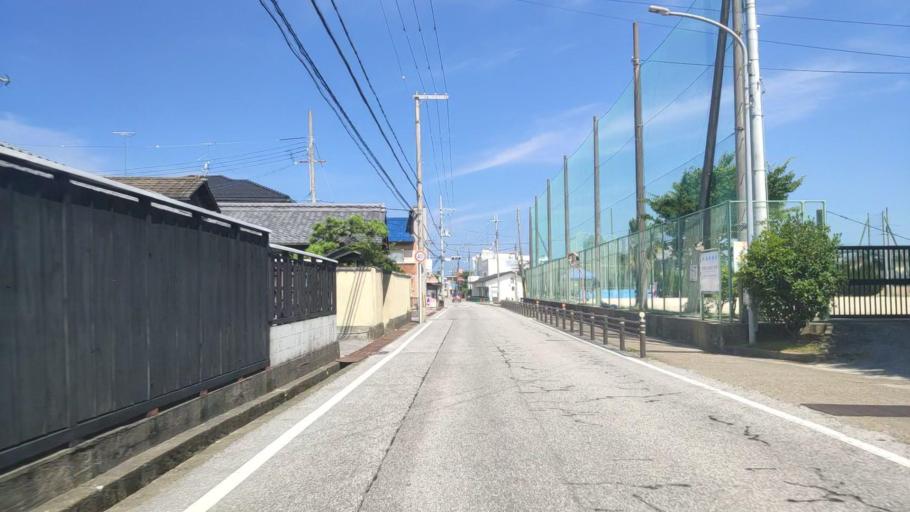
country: JP
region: Shiga Prefecture
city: Hikone
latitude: 35.2717
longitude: 136.2482
